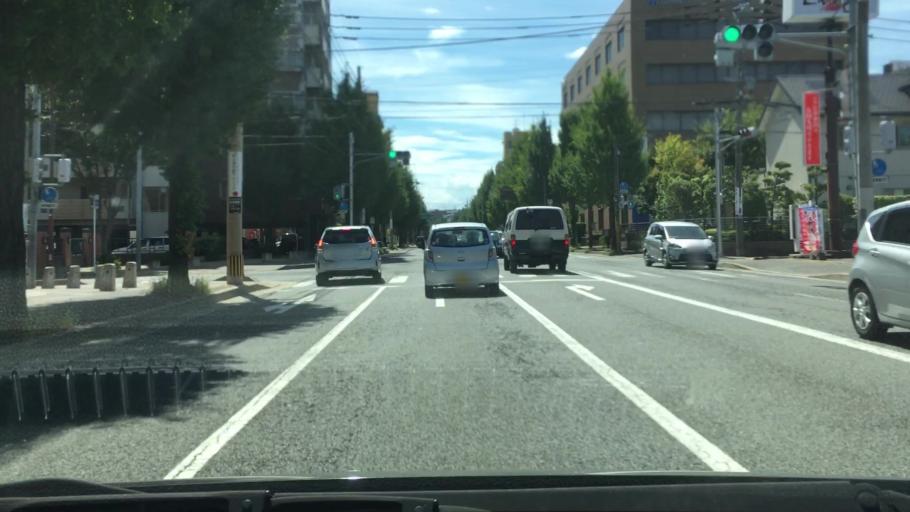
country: JP
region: Fukuoka
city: Fukuoka-shi
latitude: 33.5682
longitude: 130.4261
